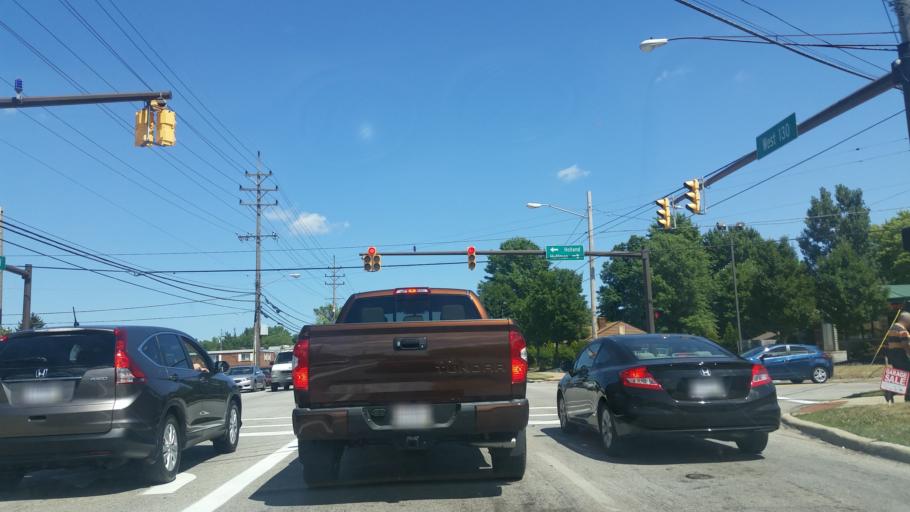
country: US
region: Ohio
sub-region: Cuyahoga County
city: Brook Park
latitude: 41.3946
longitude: -81.7844
